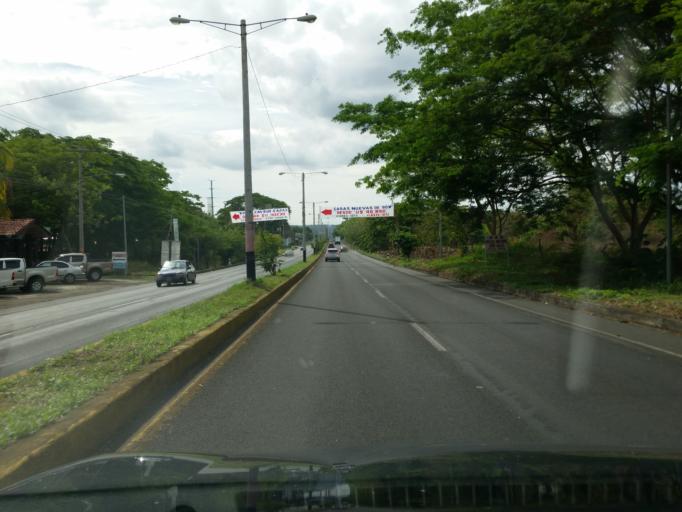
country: NI
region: Masaya
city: Ticuantepe
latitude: 12.0317
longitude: -86.1811
